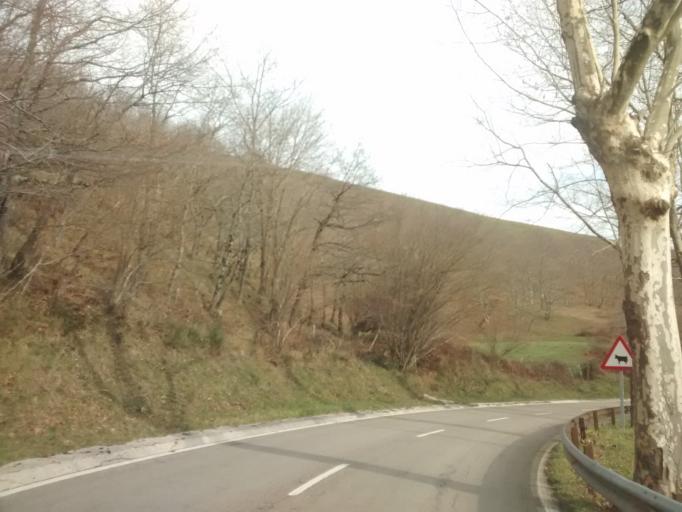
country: ES
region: Cantabria
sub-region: Provincia de Cantabria
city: Ruente
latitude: 43.2349
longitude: -4.3195
